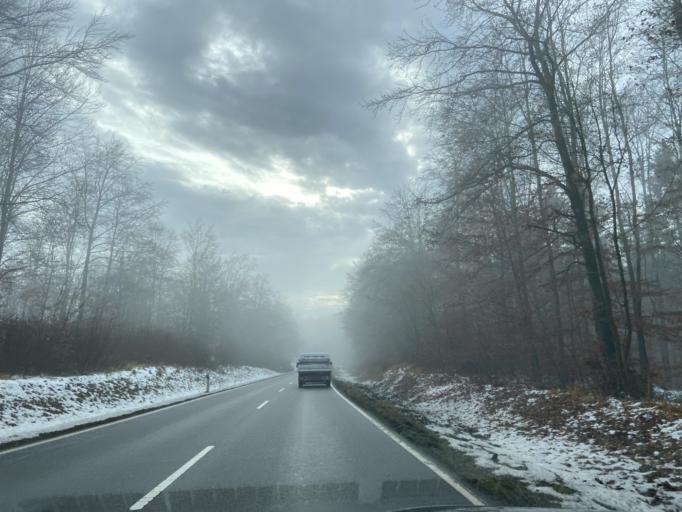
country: DE
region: Baden-Wuerttemberg
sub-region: Tuebingen Region
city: Bingen
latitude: 48.1396
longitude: 9.2608
